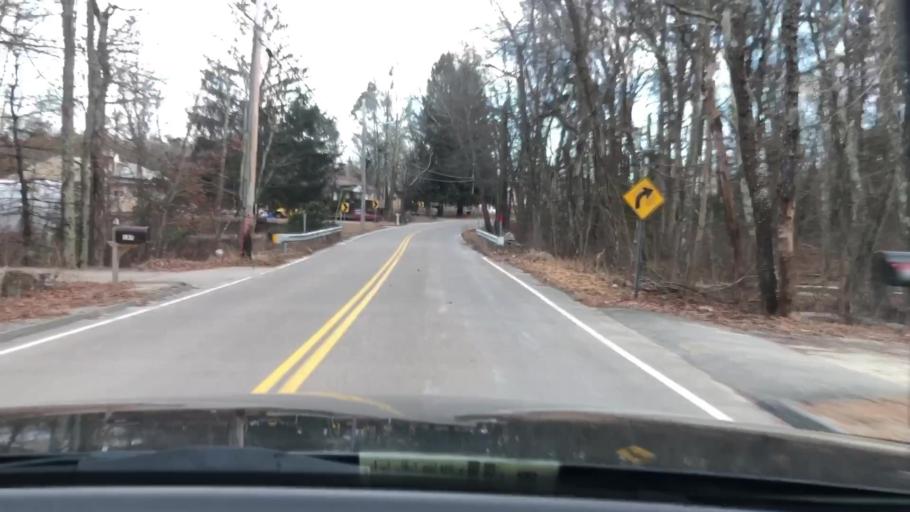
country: US
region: Massachusetts
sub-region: Worcester County
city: Blackstone
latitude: 42.0434
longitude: -71.5251
